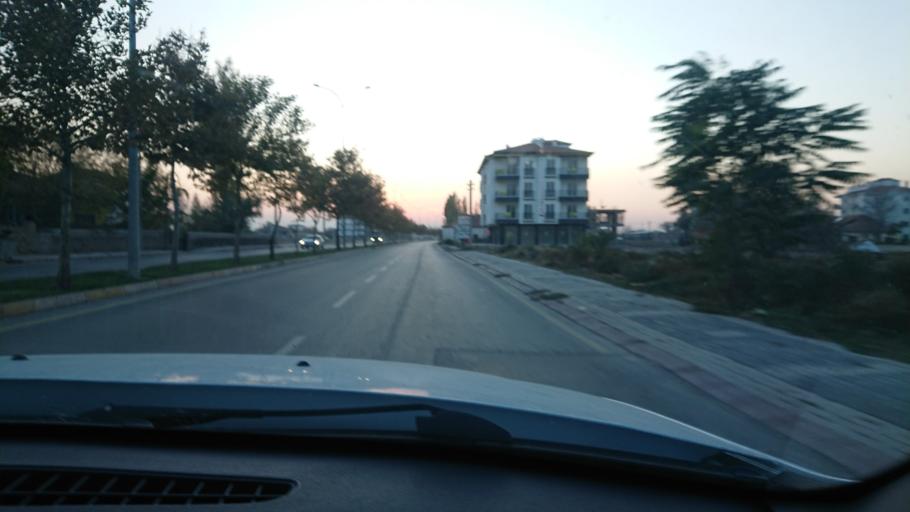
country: TR
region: Aksaray
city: Aksaray
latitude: 38.3593
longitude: 33.9972
